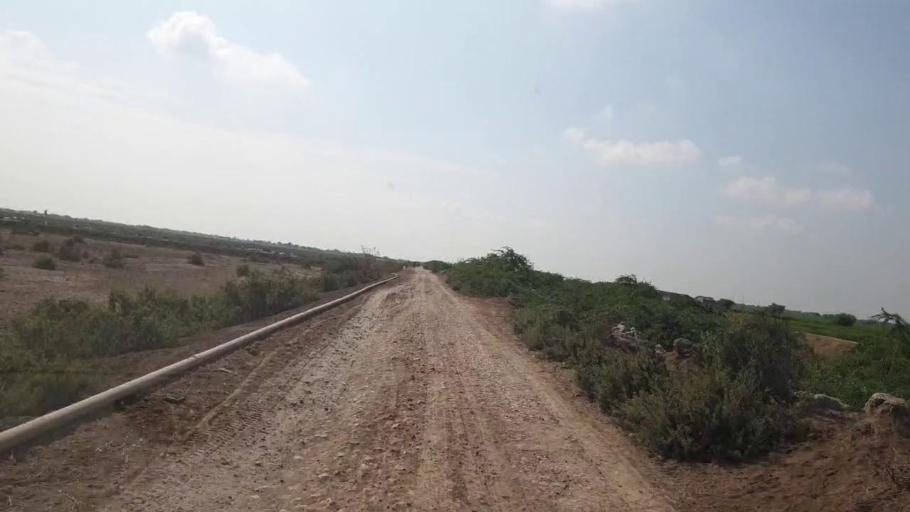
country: PK
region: Sindh
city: Badin
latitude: 24.5020
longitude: 68.6077
